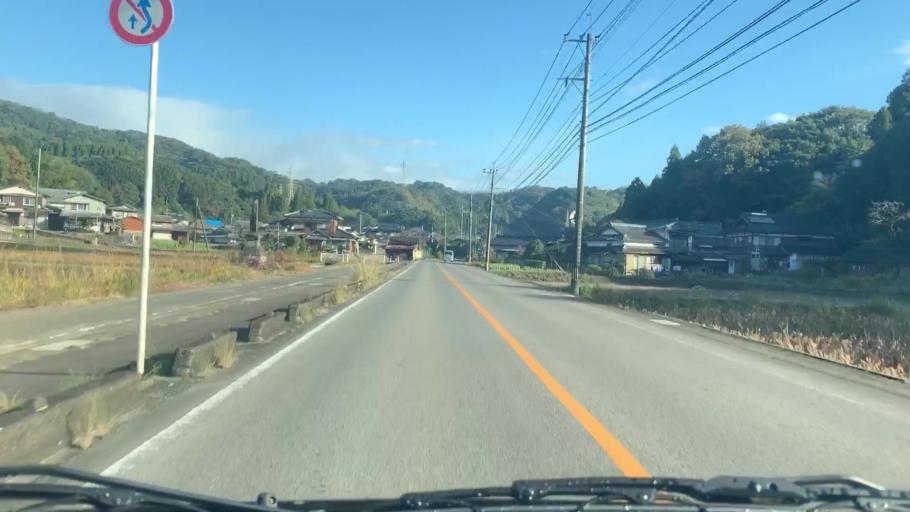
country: JP
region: Saga Prefecture
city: Takeocho-takeo
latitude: 33.2302
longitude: 130.0600
